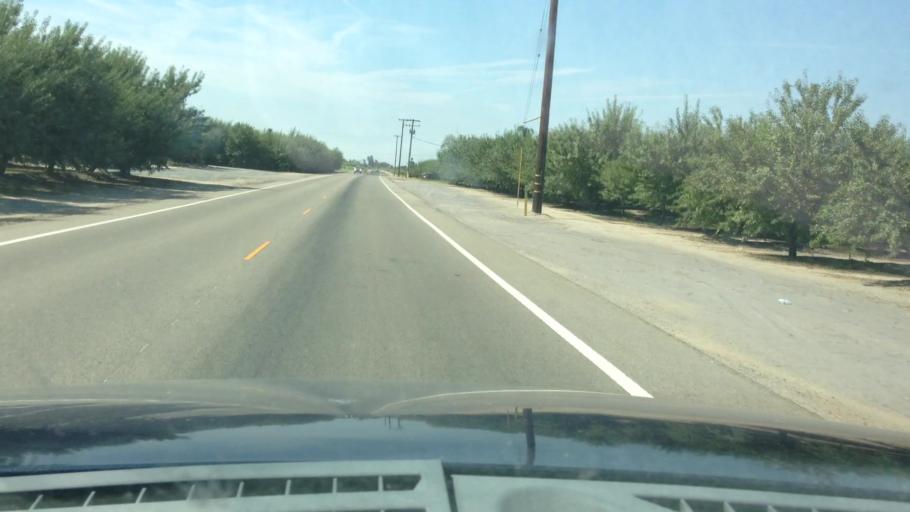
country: US
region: California
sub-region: Fresno County
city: Parlier
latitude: 36.5860
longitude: -119.5570
